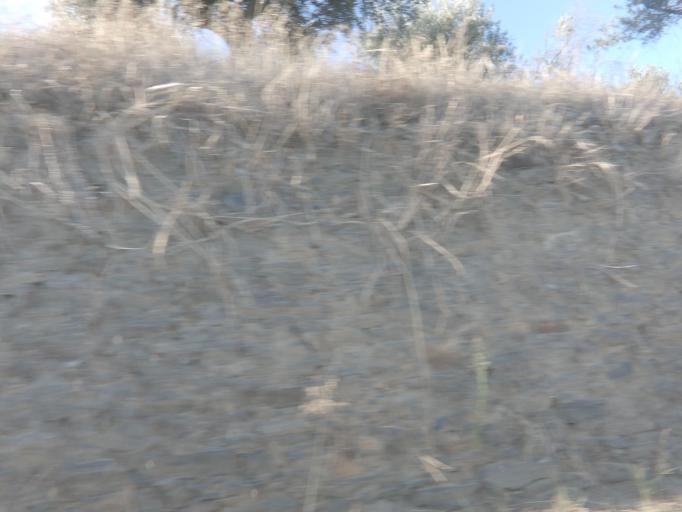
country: PT
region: Vila Real
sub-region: Peso da Regua
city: Godim
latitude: 41.1631
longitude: -7.8262
